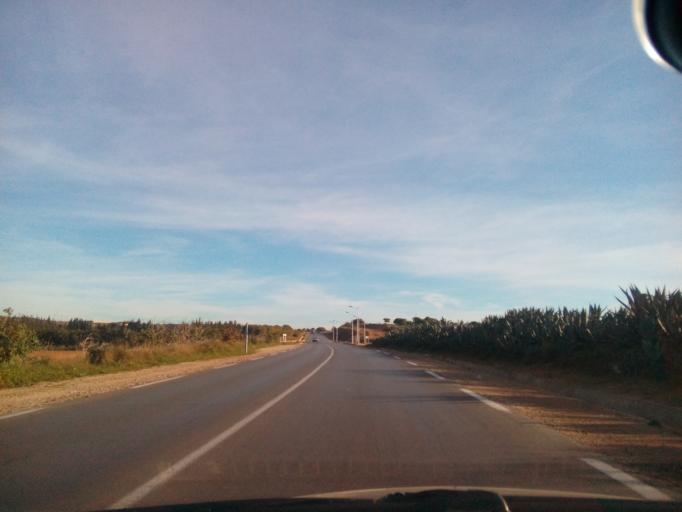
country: DZ
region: Mostaganem
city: Mostaganem
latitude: 35.8450
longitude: 0.1600
